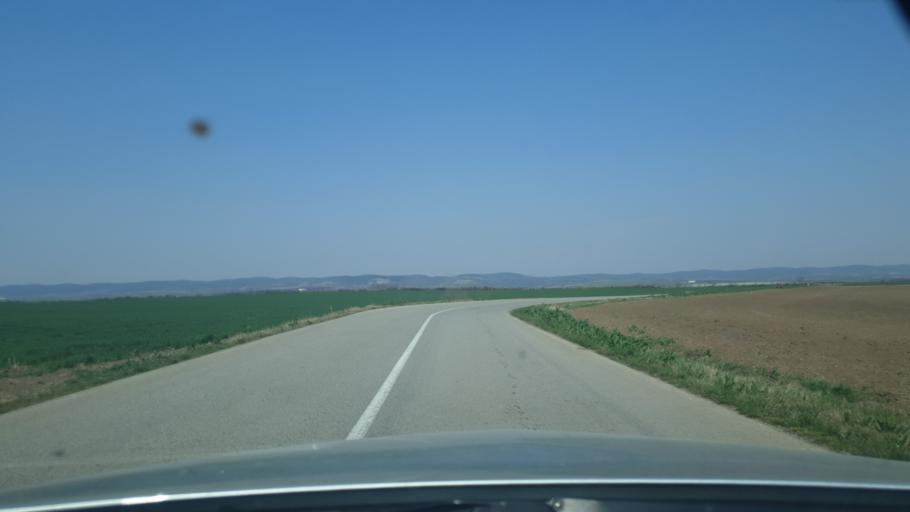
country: RS
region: Autonomna Pokrajina Vojvodina
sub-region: Sremski Okrug
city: Ruma
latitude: 45.0435
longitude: 19.7607
